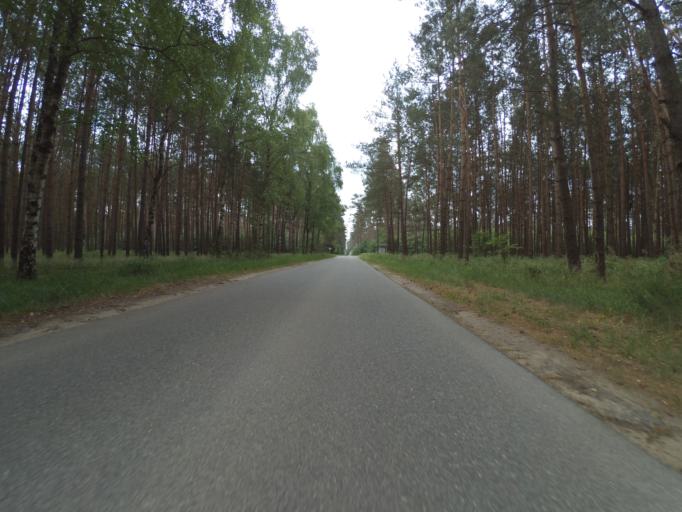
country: DE
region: Mecklenburg-Vorpommern
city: Malchow
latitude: 53.5623
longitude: 12.3685
